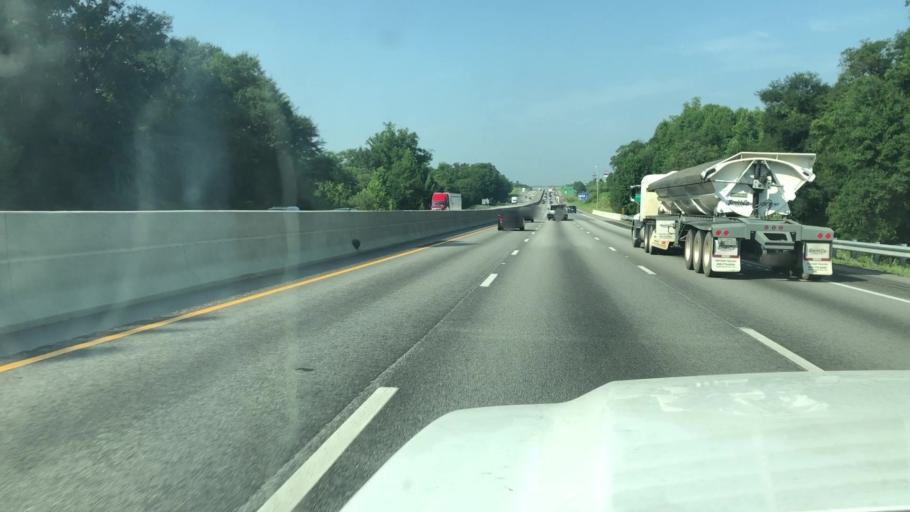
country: US
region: South Carolina
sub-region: Spartanburg County
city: Wellford
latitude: 34.9238
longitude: -82.0940
